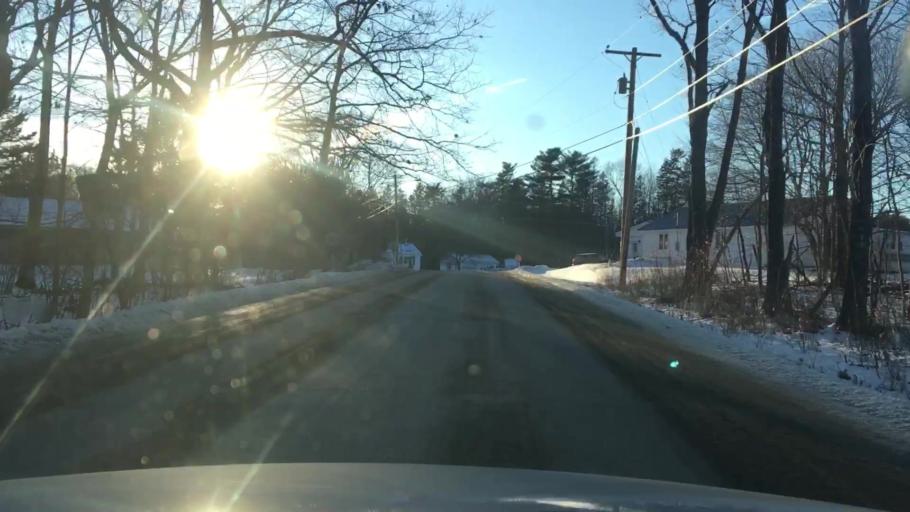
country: US
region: Maine
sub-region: Penobscot County
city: Eddington
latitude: 44.8276
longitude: -68.6560
